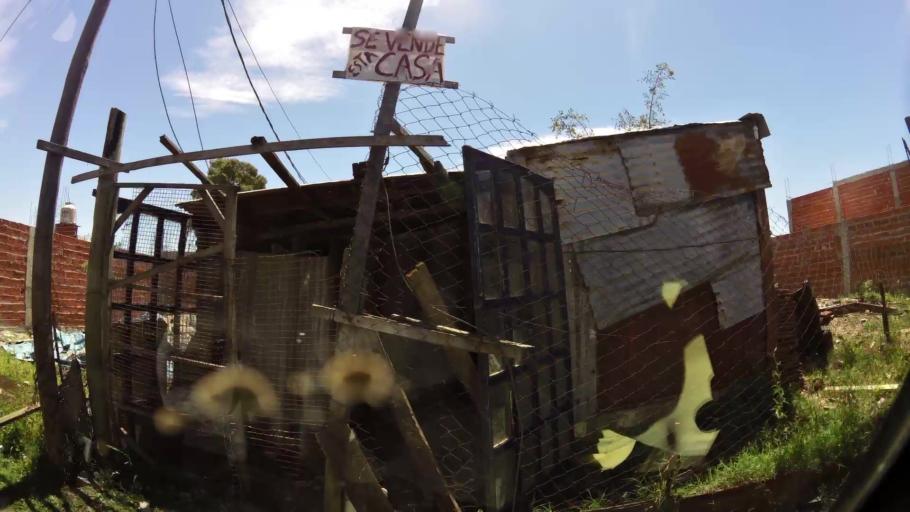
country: AR
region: Buenos Aires
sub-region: Partido de Quilmes
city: Quilmes
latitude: -34.7284
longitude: -58.3180
